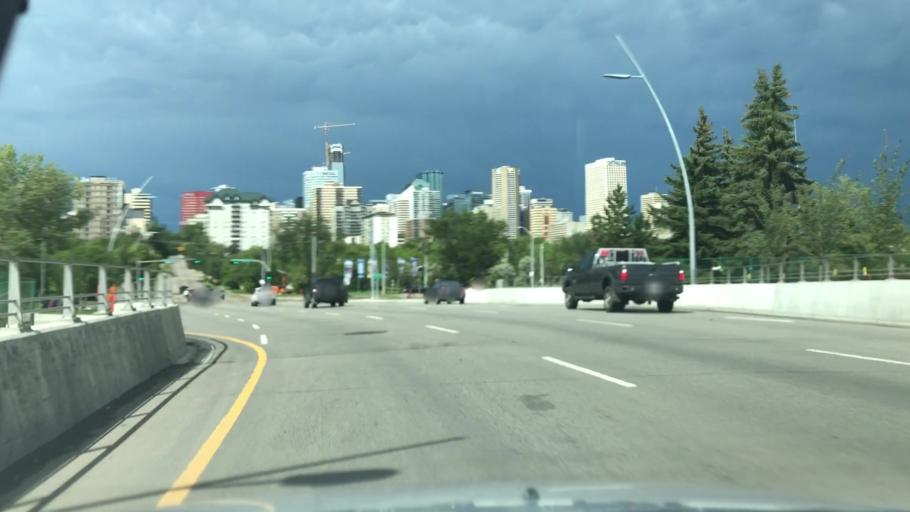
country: CA
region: Alberta
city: Edmonton
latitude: 53.5295
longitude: -113.5012
